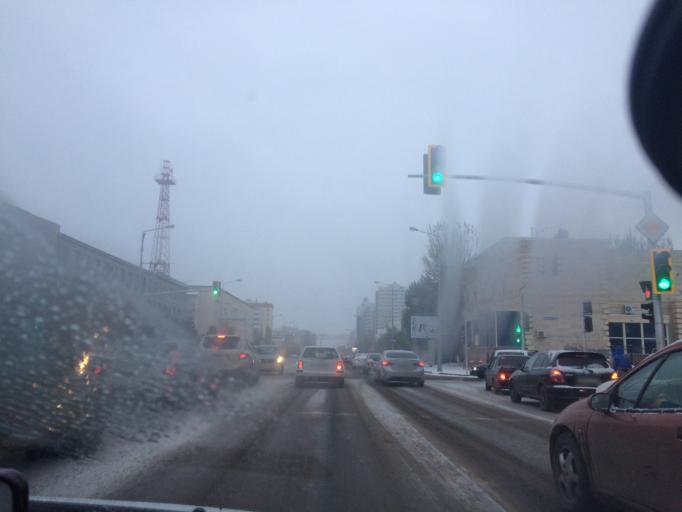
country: KZ
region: Astana Qalasy
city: Astana
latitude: 51.1727
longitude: 71.4070
